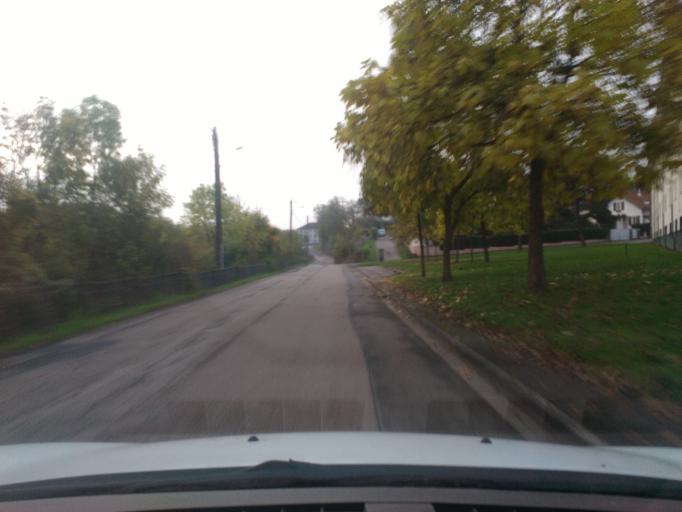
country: FR
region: Lorraine
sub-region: Departement des Vosges
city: Mirecourt
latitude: 48.3015
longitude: 6.1280
